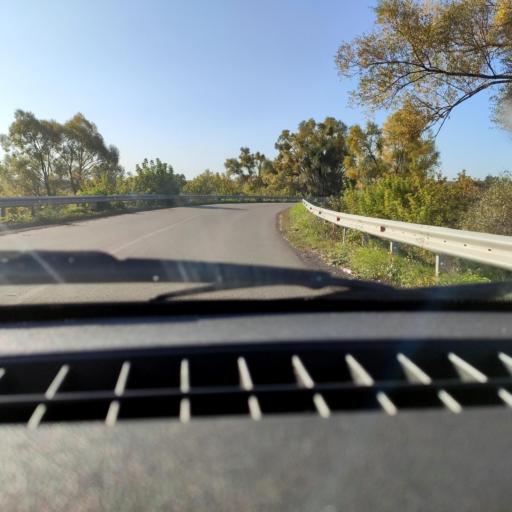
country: RU
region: Bashkortostan
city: Avdon
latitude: 54.5589
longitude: 55.7636
